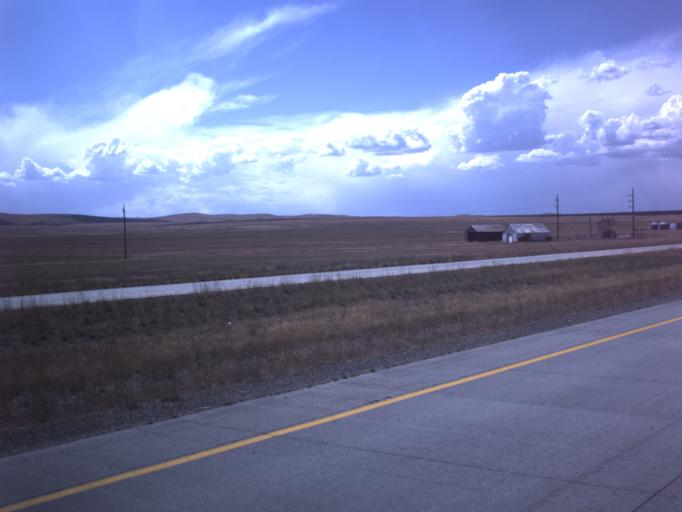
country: US
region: Utah
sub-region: Box Elder County
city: Garland
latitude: 41.8600
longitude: -112.4542
